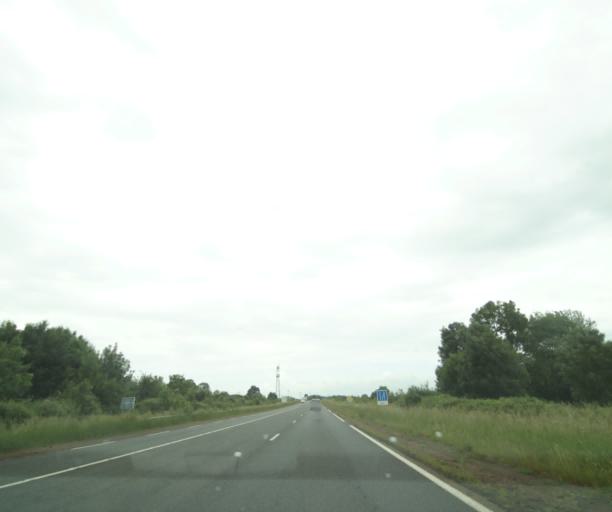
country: FR
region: Poitou-Charentes
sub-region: Departement des Deux-Sevres
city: Saint-Varent
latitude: 46.8328
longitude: -0.2067
